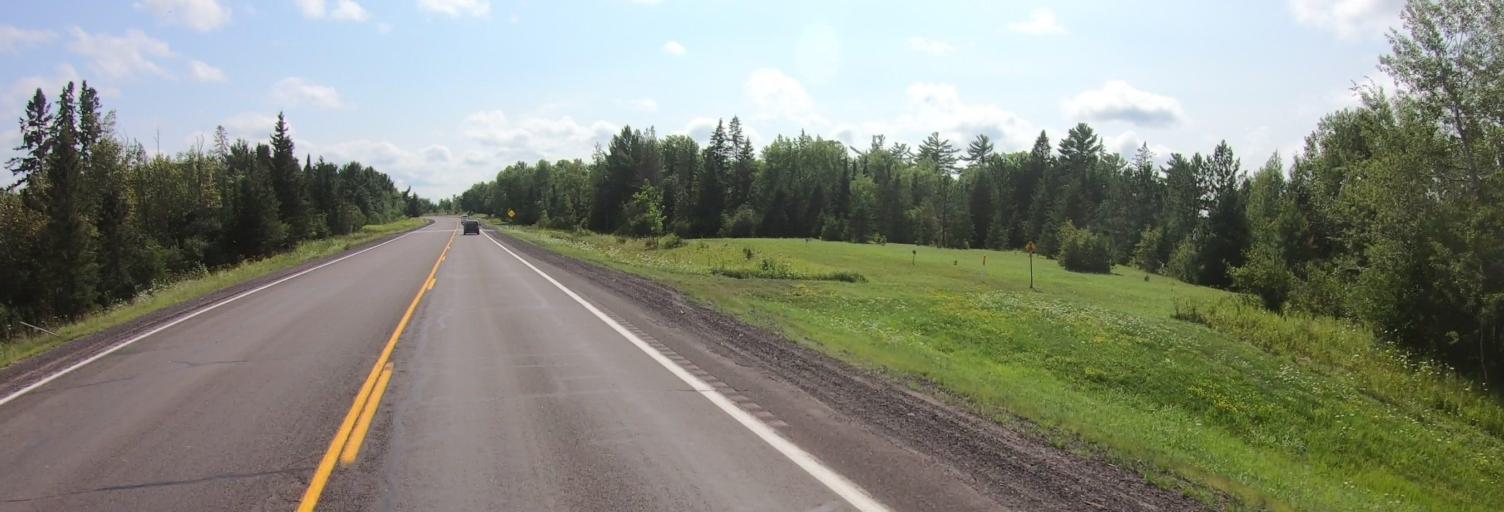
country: US
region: Michigan
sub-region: Ontonagon County
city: Ontonagon
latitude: 46.7208
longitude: -89.1550
